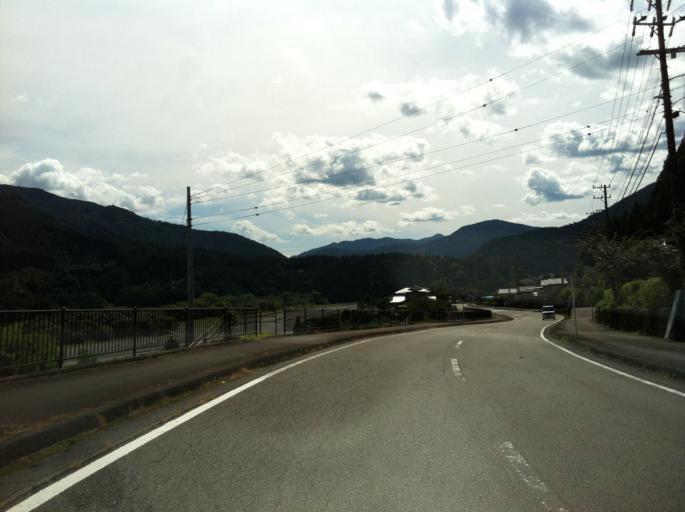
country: JP
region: Shizuoka
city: Kanaya
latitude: 35.0660
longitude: 138.1043
